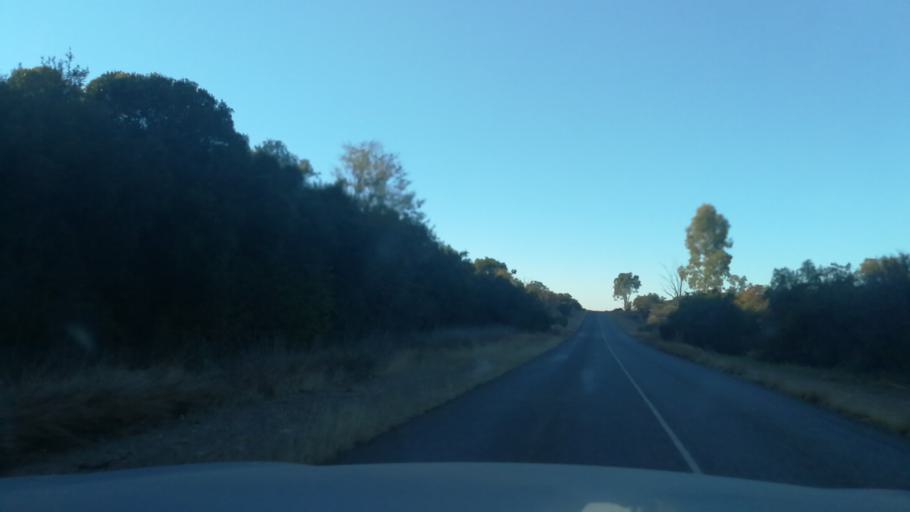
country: ZA
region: North-West
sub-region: Bojanala Platinum District Municipality
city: Koster
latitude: -25.6570
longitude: 26.7144
